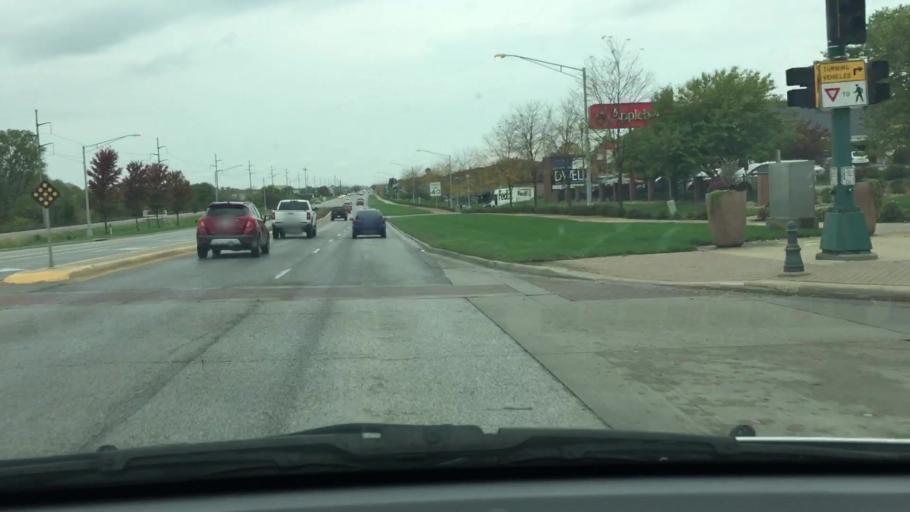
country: US
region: Iowa
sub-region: Johnson County
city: Coralville
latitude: 41.6754
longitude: -91.5823
